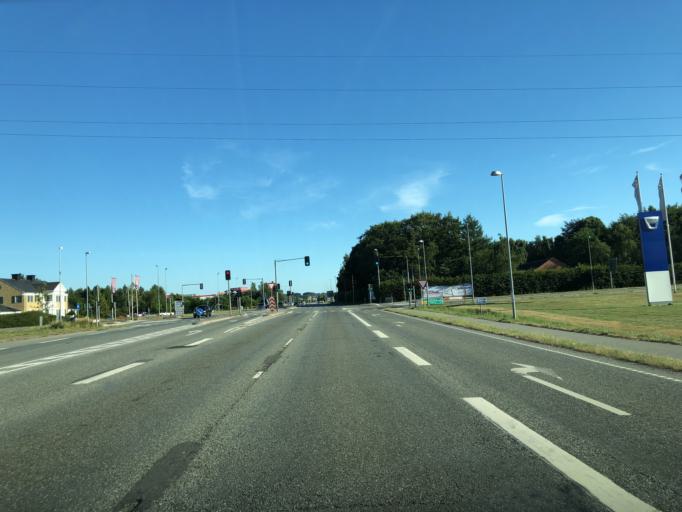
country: DK
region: Central Jutland
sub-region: Randers Kommune
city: Randers
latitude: 56.4344
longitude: 10.0526
